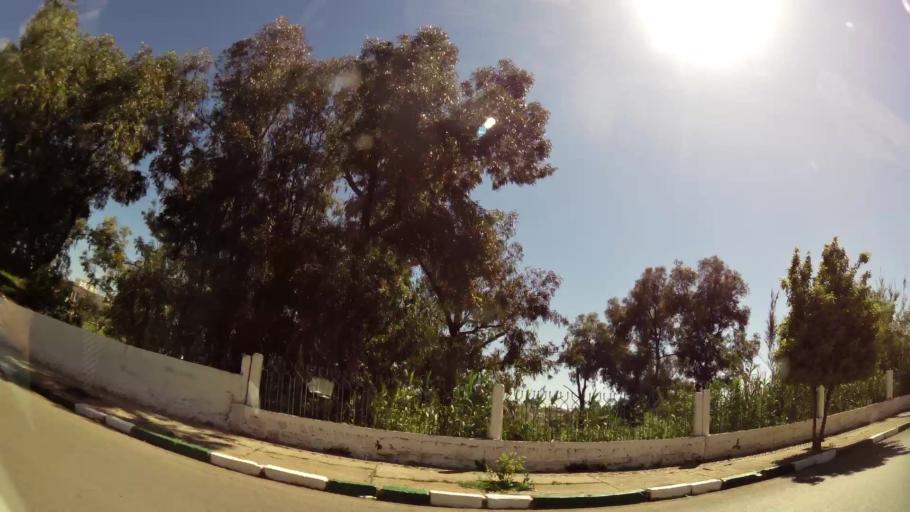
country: MA
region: Meknes-Tafilalet
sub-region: Meknes
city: Meknes
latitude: 33.8915
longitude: -5.5532
